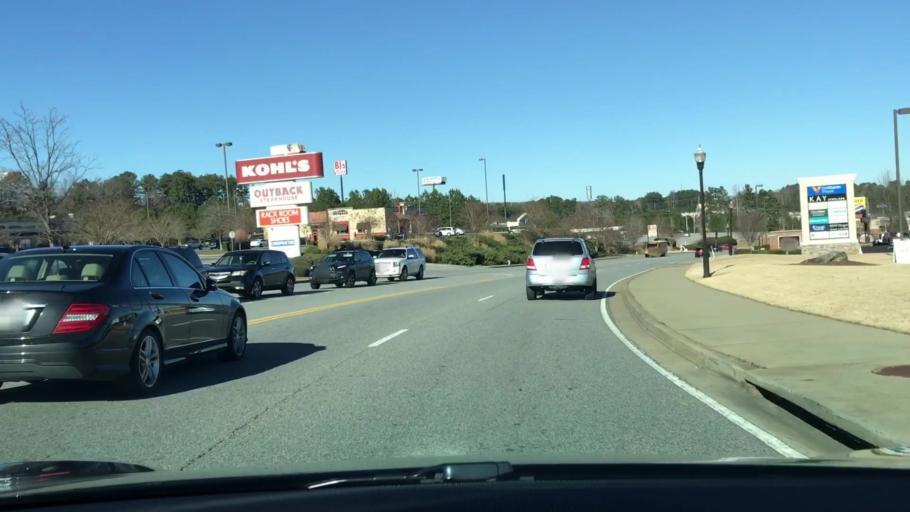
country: US
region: Georgia
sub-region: Forsyth County
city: Cumming
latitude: 34.1875
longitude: -84.1327
